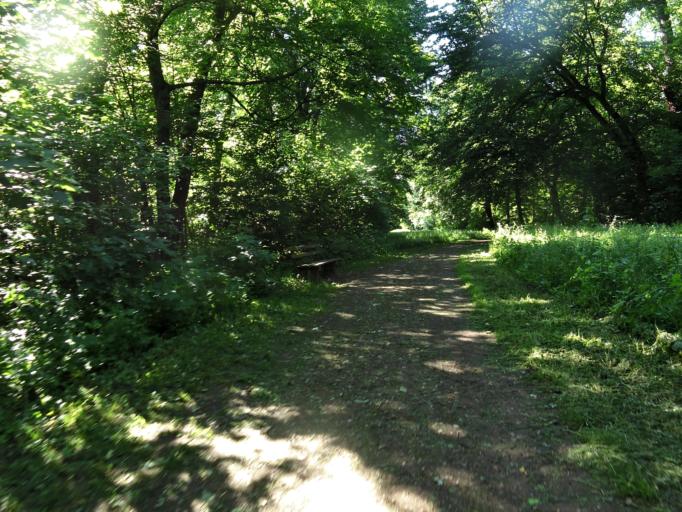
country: DE
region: Saxony
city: Leipzig
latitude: 51.3529
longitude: 12.3582
